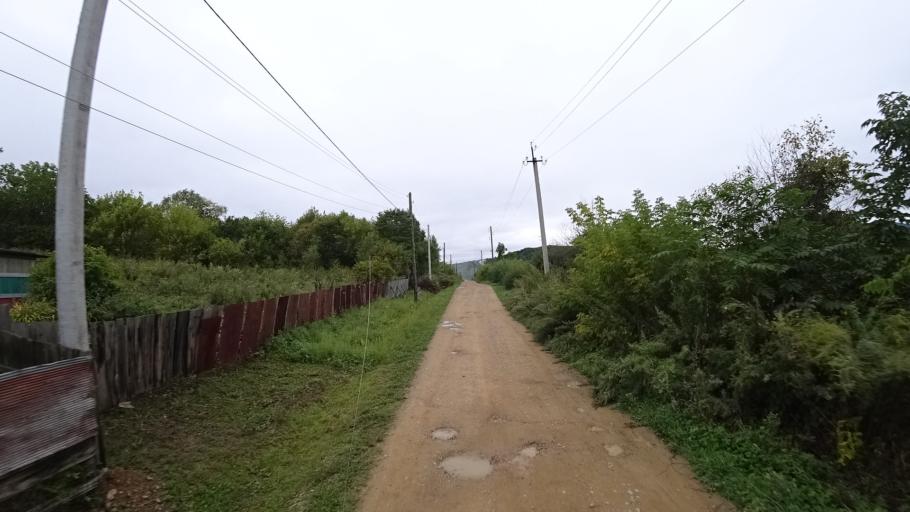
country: RU
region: Primorskiy
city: Rettikhovka
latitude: 44.1740
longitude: 132.8839
